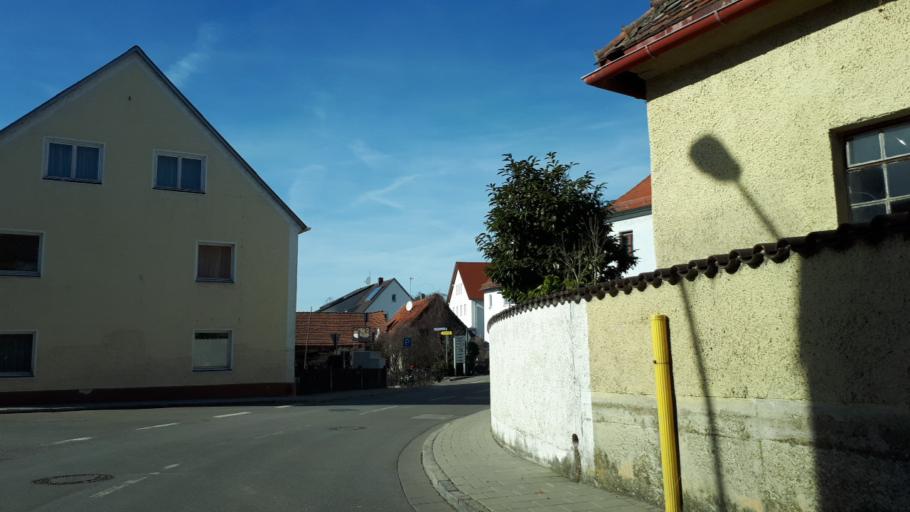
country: DE
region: Bavaria
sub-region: Upper Palatinate
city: Pentling
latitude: 48.9814
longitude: 12.0584
